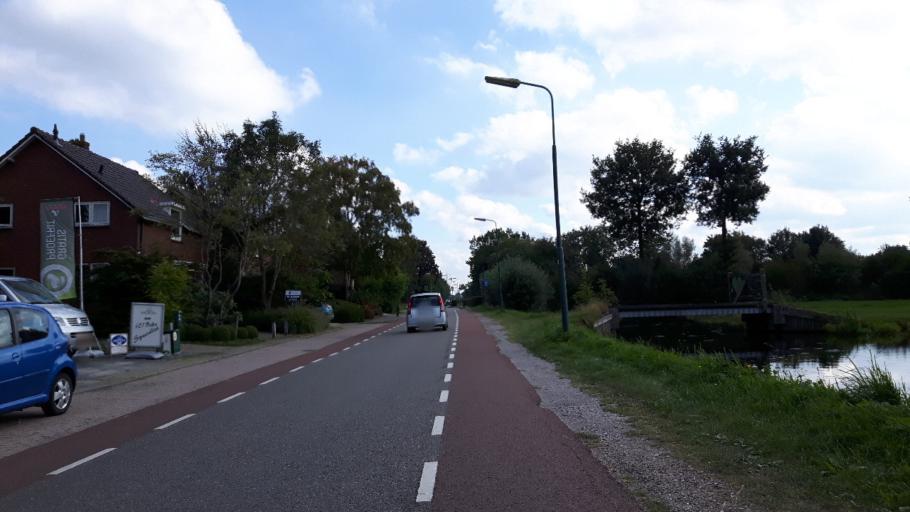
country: NL
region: Utrecht
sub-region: Stichtse Vecht
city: Breukelen
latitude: 52.1563
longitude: 4.9631
